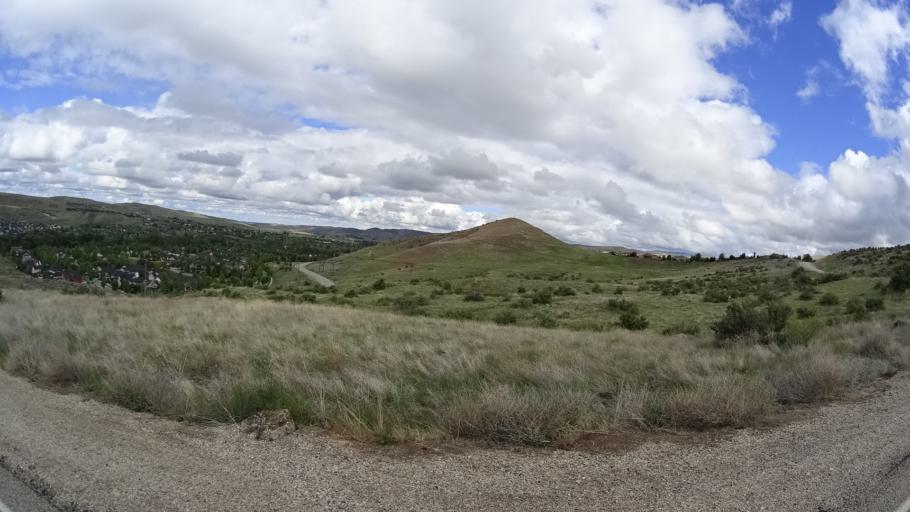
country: US
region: Idaho
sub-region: Ada County
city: Garden City
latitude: 43.7201
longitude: -116.2347
